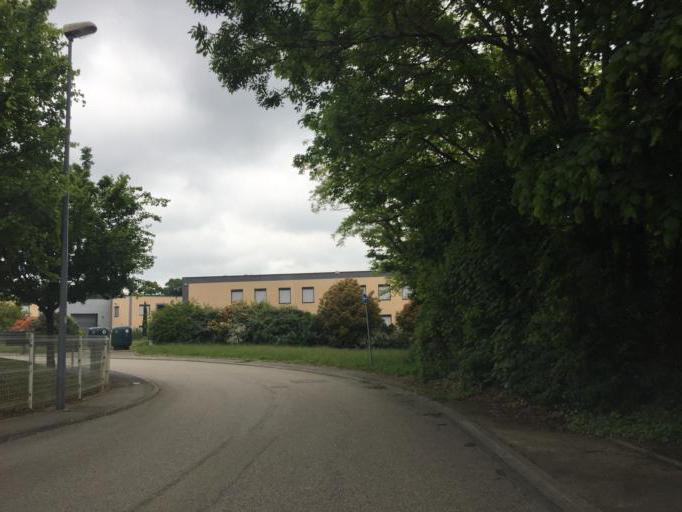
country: FR
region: Rhone-Alpes
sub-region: Departement du Rhone
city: Rillieux-la-Pape
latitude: 45.8205
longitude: 4.9237
